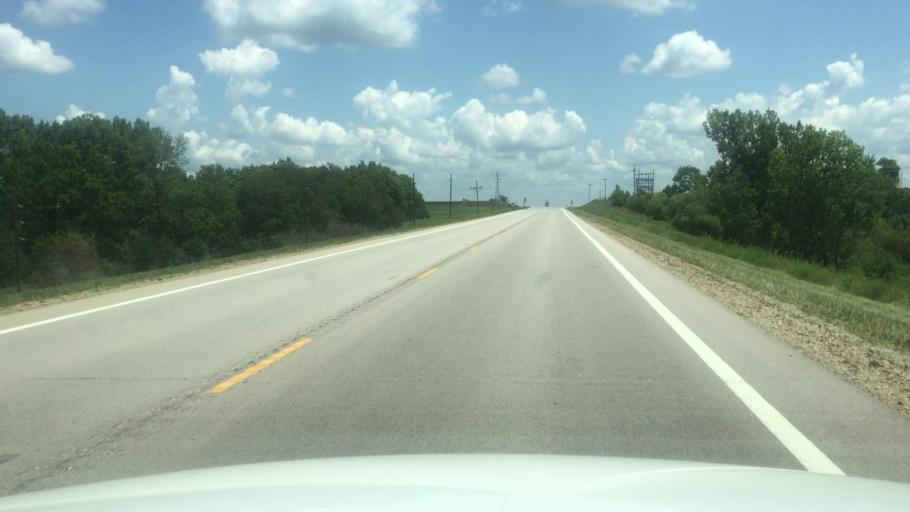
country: US
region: Kansas
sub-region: Brown County
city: Horton
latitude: 39.6675
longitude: -95.4943
